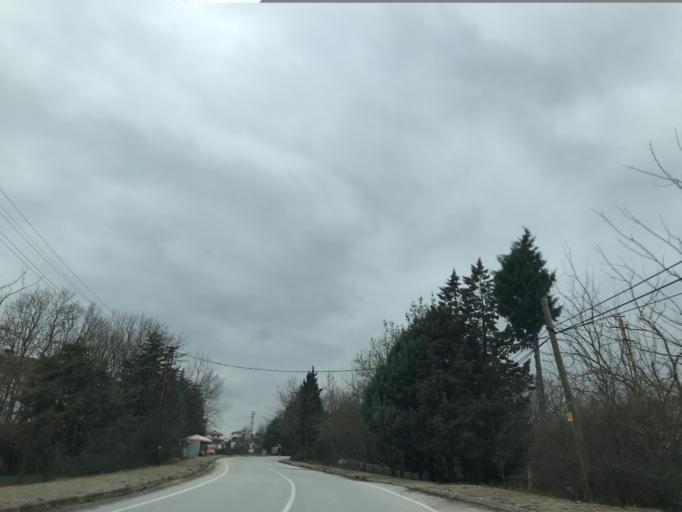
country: TR
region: Yalova
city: Termal
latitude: 40.6078
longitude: 29.2007
